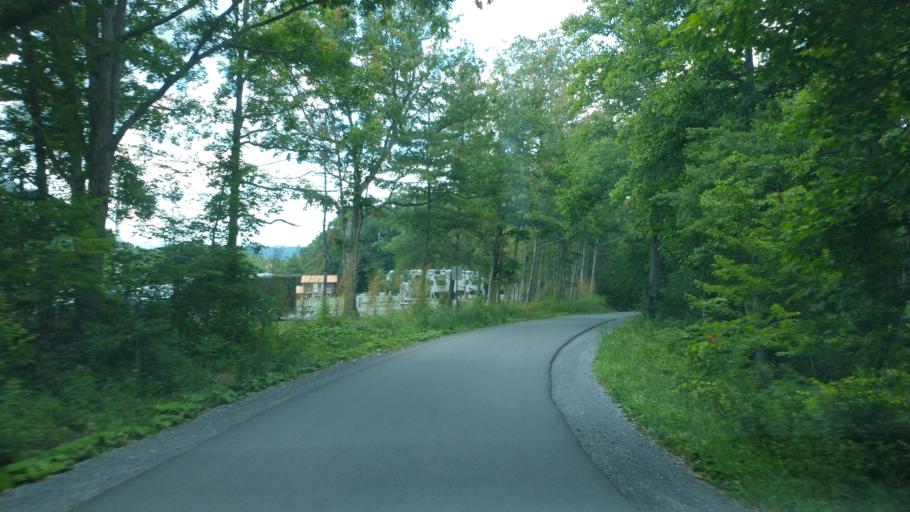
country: US
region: West Virginia
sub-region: Mercer County
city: Athens
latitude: 37.4516
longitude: -81.0620
